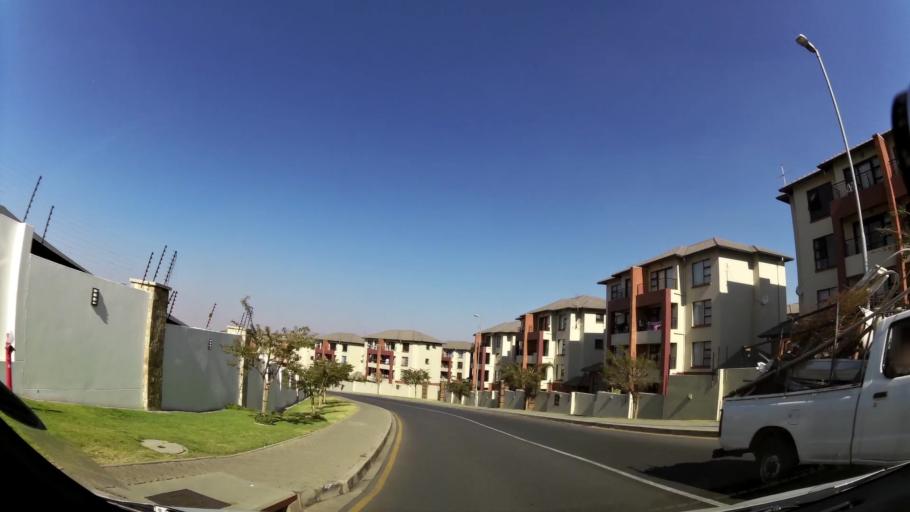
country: ZA
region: Gauteng
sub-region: City of Johannesburg Metropolitan Municipality
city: Johannesburg
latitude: -26.2648
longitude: 28.0367
